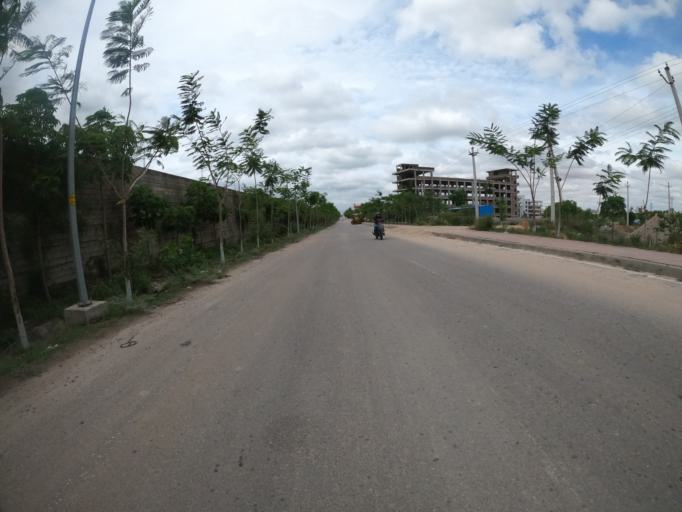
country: IN
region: Telangana
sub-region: Rangareddi
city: Sriramnagar
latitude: 17.2684
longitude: 78.3786
